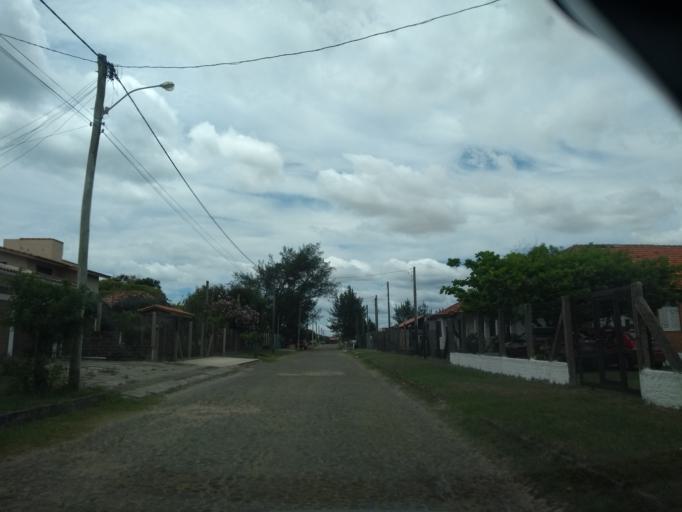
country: BR
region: Rio Grande do Sul
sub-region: Tramandai
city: Tramandai
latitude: -30.0656
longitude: -50.1618
